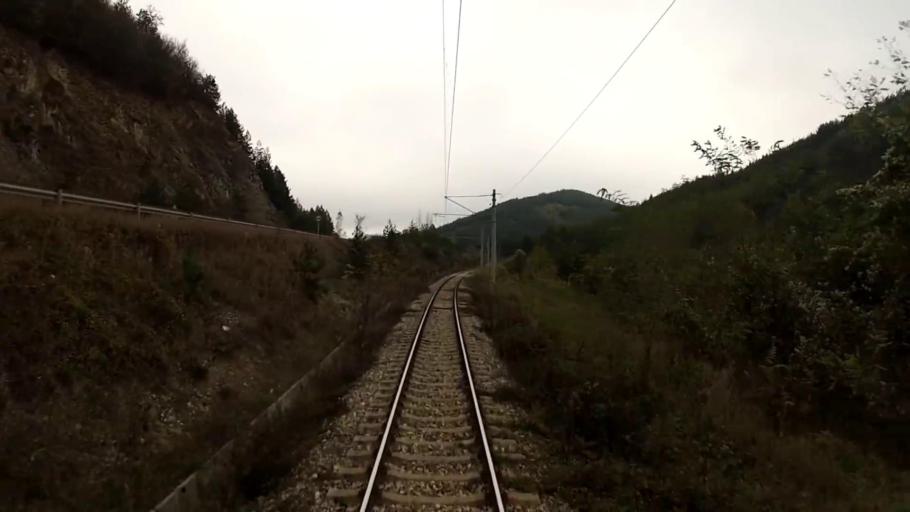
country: BG
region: Sofiya
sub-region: Obshtina Dragoman
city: Dragoman
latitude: 42.9490
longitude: 22.9022
